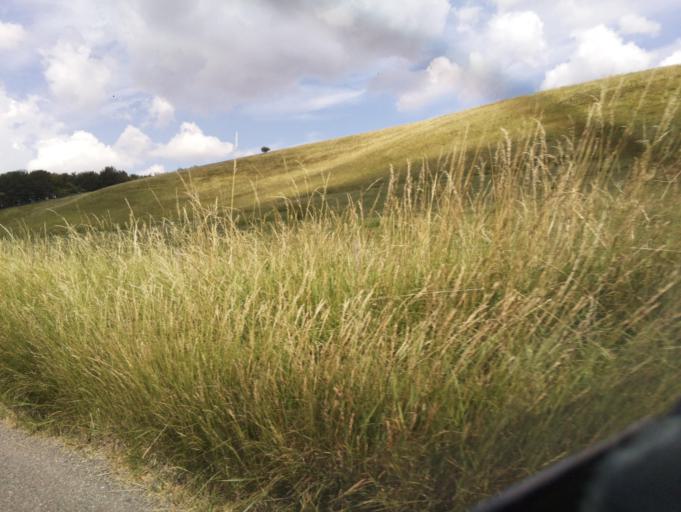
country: GB
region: England
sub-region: Borough of Swindon
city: Bishopstone
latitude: 51.5406
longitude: -1.5919
